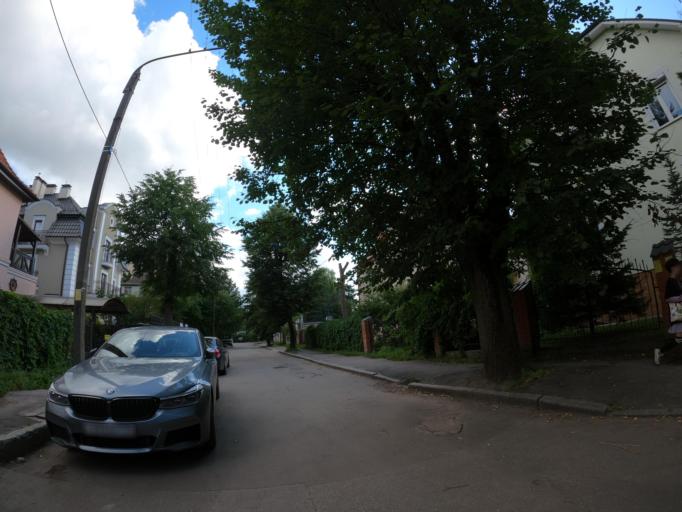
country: RU
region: Kaliningrad
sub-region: Gorod Kaliningrad
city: Kaliningrad
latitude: 54.7312
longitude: 20.4726
